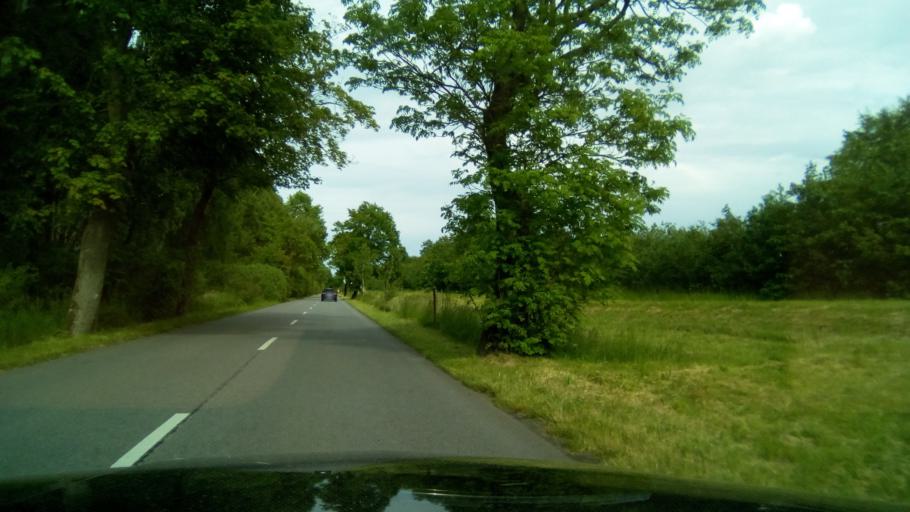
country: PL
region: Pomeranian Voivodeship
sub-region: Powiat pucki
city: Wierzchucino
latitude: 54.7953
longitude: 18.0370
